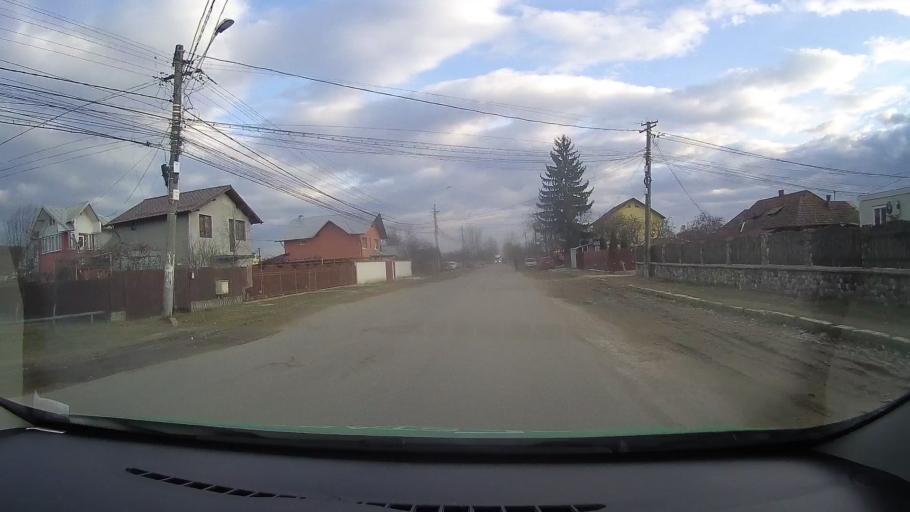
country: RO
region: Dambovita
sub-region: Municipiul Moreni
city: Moreni
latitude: 44.9677
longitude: 25.6531
